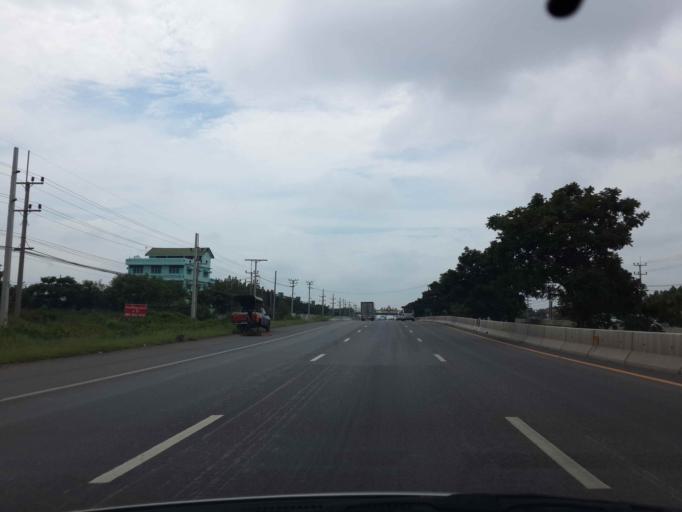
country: TH
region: Samut Songkhram
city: Samut Songkhram
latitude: 13.4318
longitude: 100.0498
